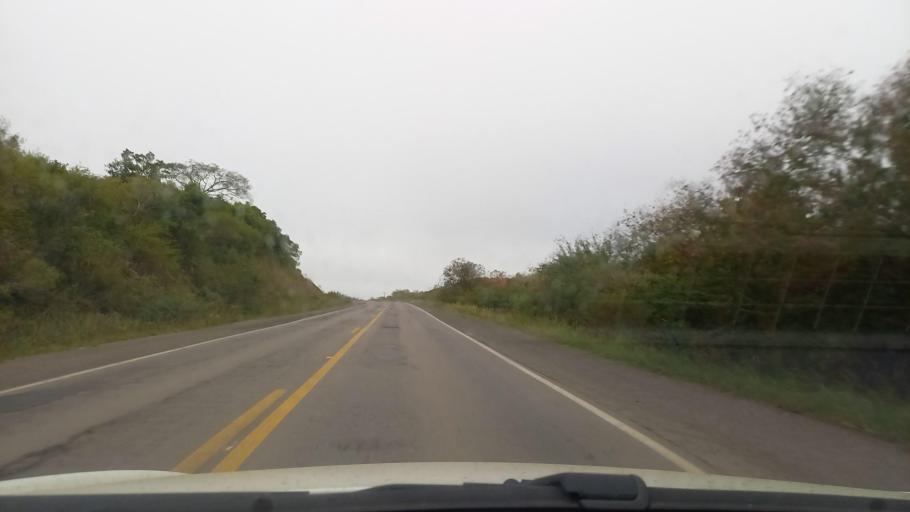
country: BR
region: Rio Grande do Sul
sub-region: Rosario Do Sul
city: Rosario do Sul
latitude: -30.1240
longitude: -54.6490
